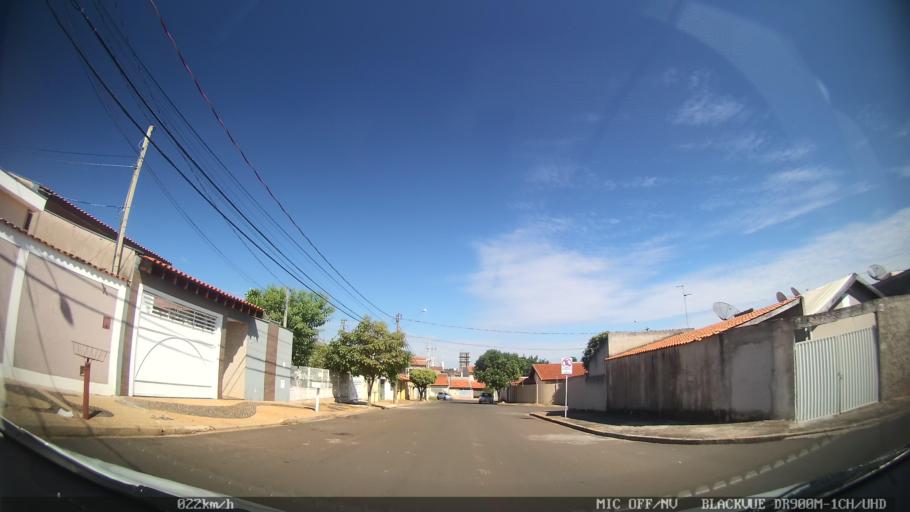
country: BR
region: Sao Paulo
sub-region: Santa Barbara D'Oeste
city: Santa Barbara d'Oeste
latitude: -22.7441
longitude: -47.4108
